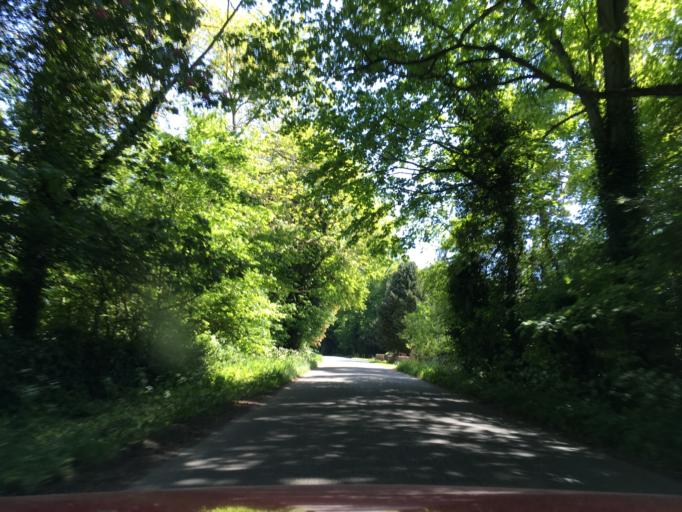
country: GB
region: England
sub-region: Gloucestershire
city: Coates
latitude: 51.6992
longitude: -2.0242
